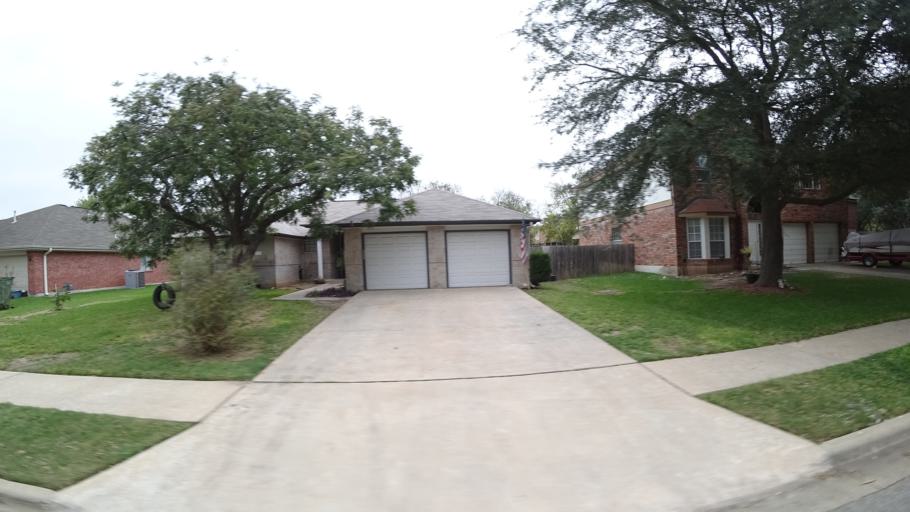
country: US
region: Texas
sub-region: Travis County
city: Pflugerville
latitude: 30.4494
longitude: -97.6155
